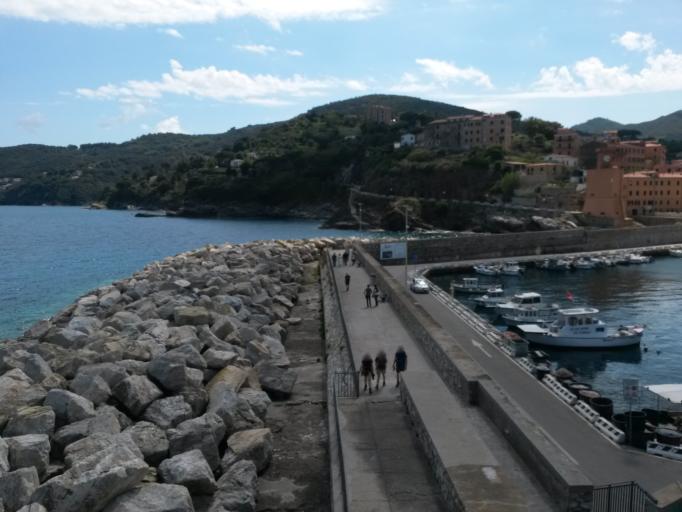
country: IT
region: Tuscany
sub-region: Provincia di Livorno
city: Rio Marina
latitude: 42.8152
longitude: 10.4313
